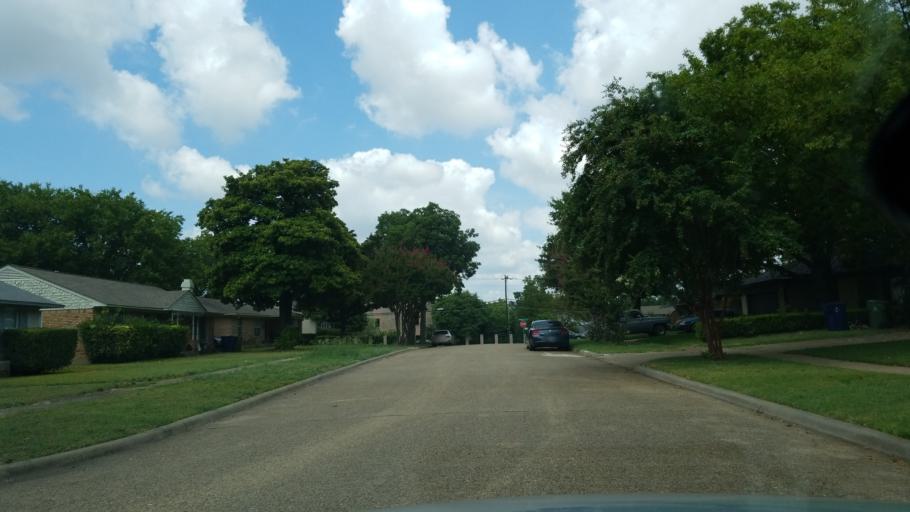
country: US
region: Texas
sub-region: Dallas County
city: Garland
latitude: 32.9154
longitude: -96.6568
